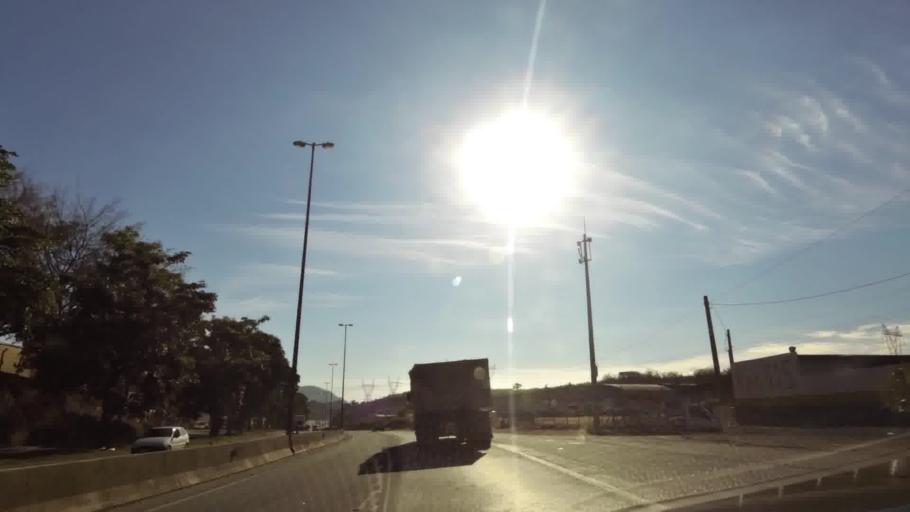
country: BR
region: Espirito Santo
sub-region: Viana
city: Viana
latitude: -20.3627
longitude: -40.4369
